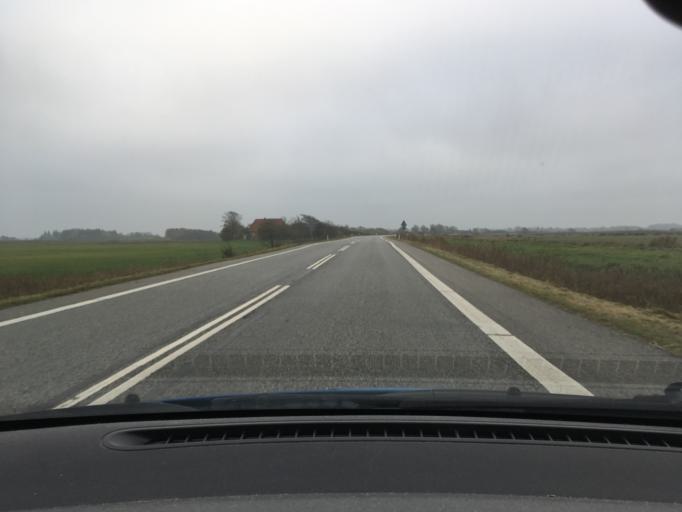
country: DE
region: Schleswig-Holstein
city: Aventoft
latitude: 54.9195
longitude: 8.8334
